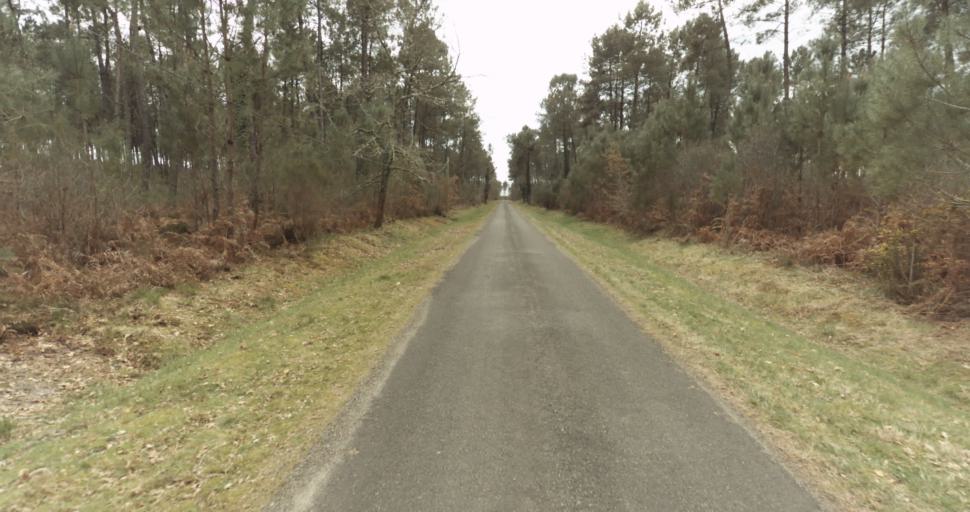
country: FR
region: Aquitaine
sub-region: Departement des Landes
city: Roquefort
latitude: 44.0561
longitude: -0.3778
